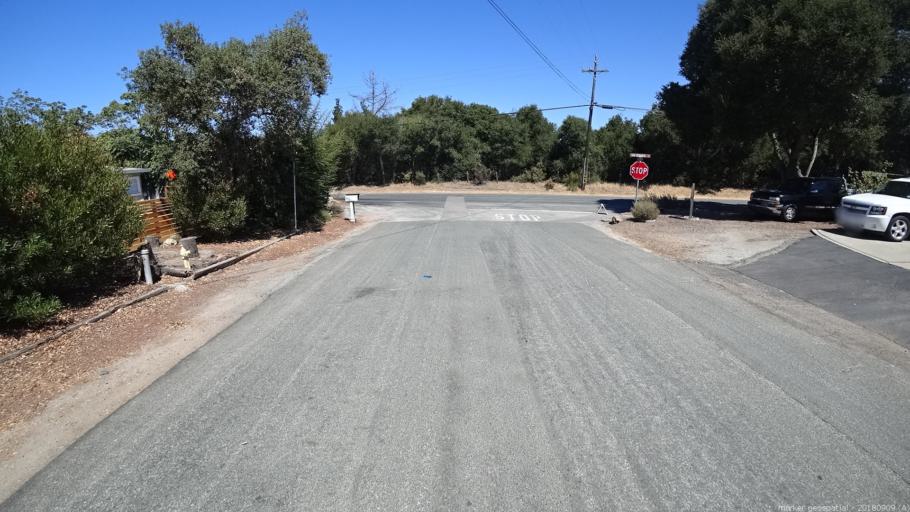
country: US
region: California
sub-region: Monterey County
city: Carmel Valley Village
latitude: 36.5783
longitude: -121.7198
